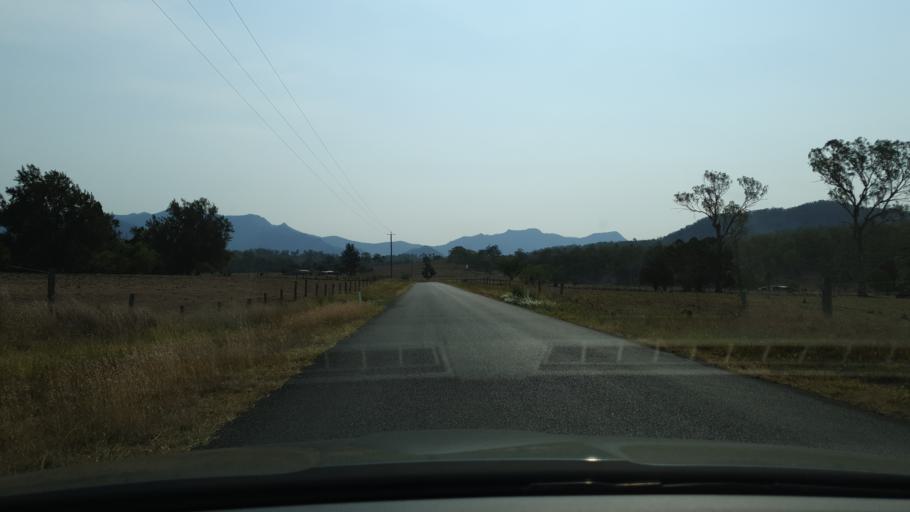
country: AU
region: Queensland
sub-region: Ipswich
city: Deebing Heights
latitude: -28.1386
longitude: 152.5747
